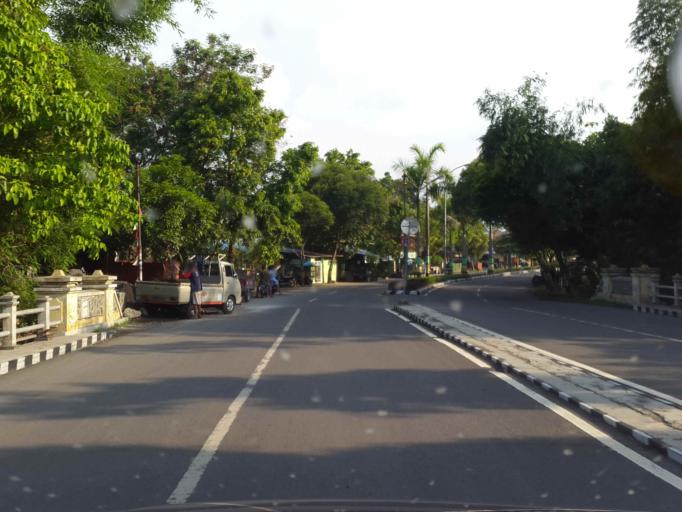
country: ID
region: Central Java
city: Slawi
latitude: -6.9862
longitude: 109.1270
